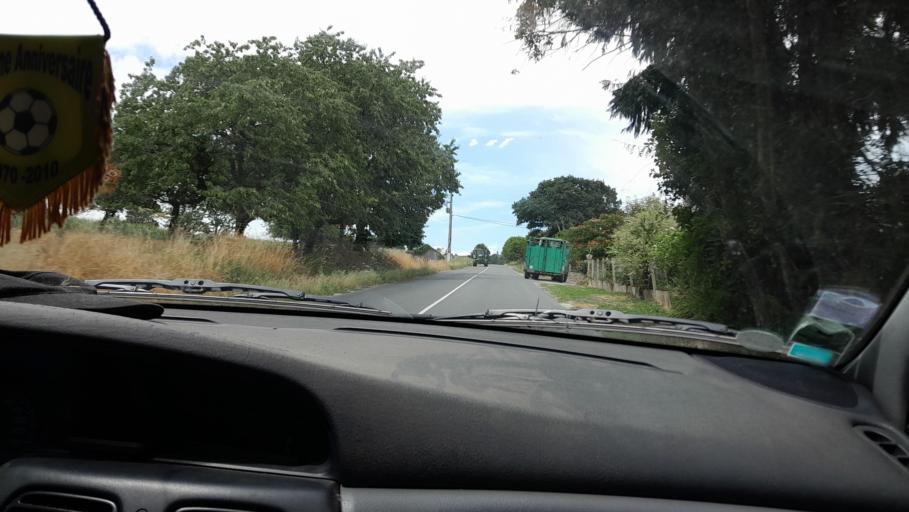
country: FR
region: Pays de la Loire
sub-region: Departement de la Mayenne
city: Juvigne
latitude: 48.1982
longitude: -1.0445
